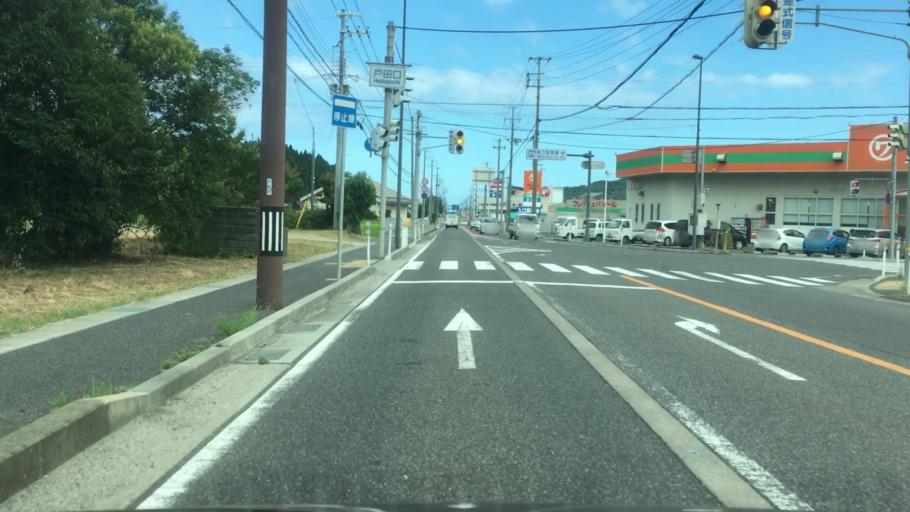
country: JP
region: Tottori
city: Tottori
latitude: 35.6144
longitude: 134.4664
